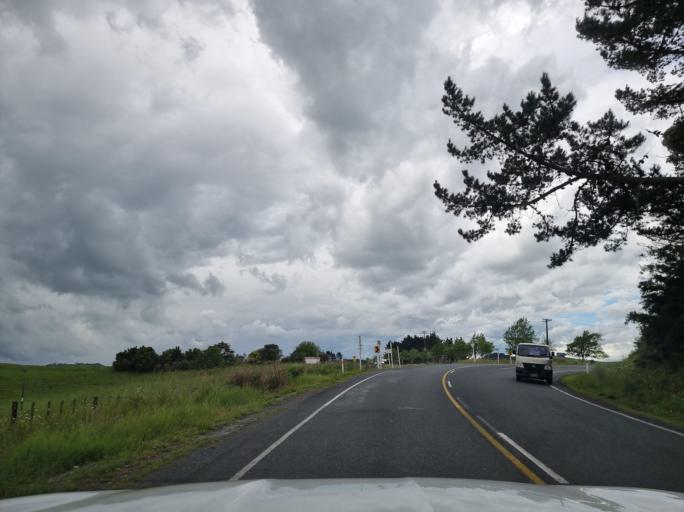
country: NZ
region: Northland
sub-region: Whangarei
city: Maungatapere
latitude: -35.8598
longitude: 174.2503
